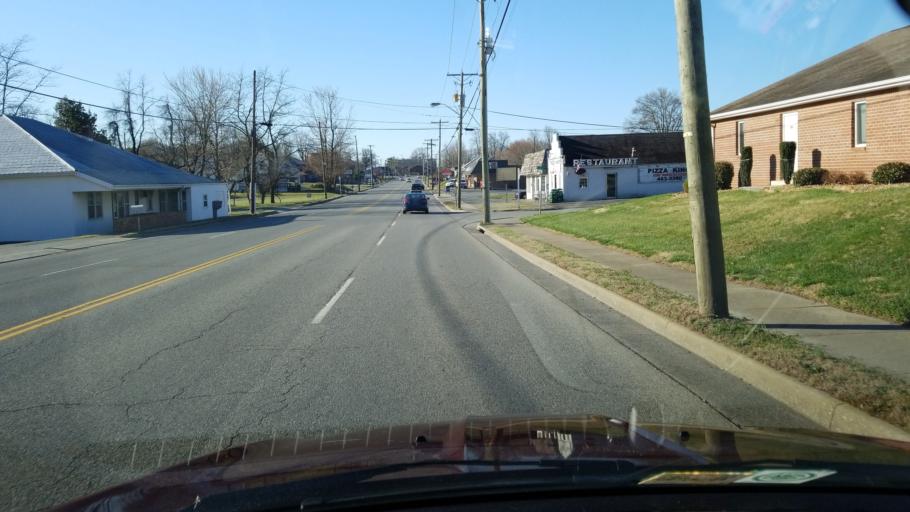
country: US
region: Virginia
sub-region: Franklin County
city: Rocky Mount
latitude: 37.0088
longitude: -79.8942
